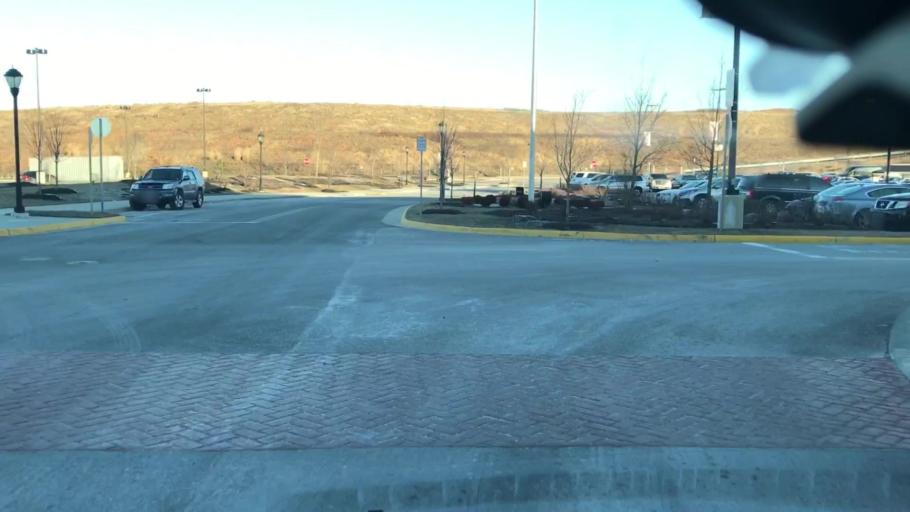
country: US
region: Virginia
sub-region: Fairfax County
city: Newington
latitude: 38.7427
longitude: -77.1620
